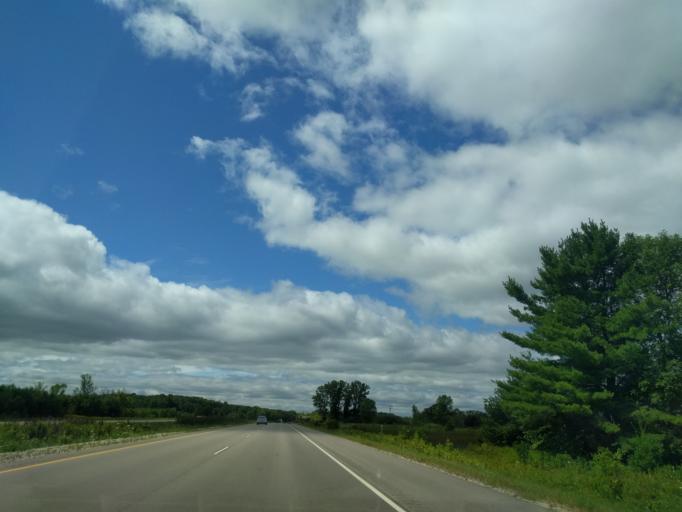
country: US
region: Wisconsin
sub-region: Oconto County
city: Oconto
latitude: 44.8057
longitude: -87.9740
